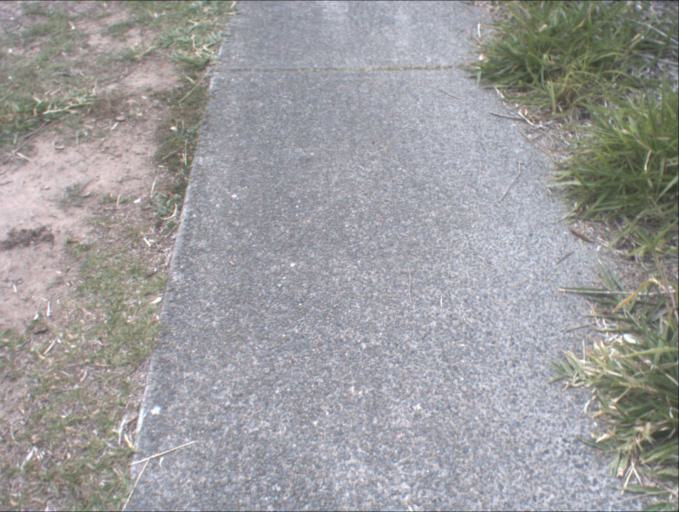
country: AU
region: Queensland
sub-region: Logan
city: Park Ridge South
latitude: -27.6694
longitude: 153.0342
